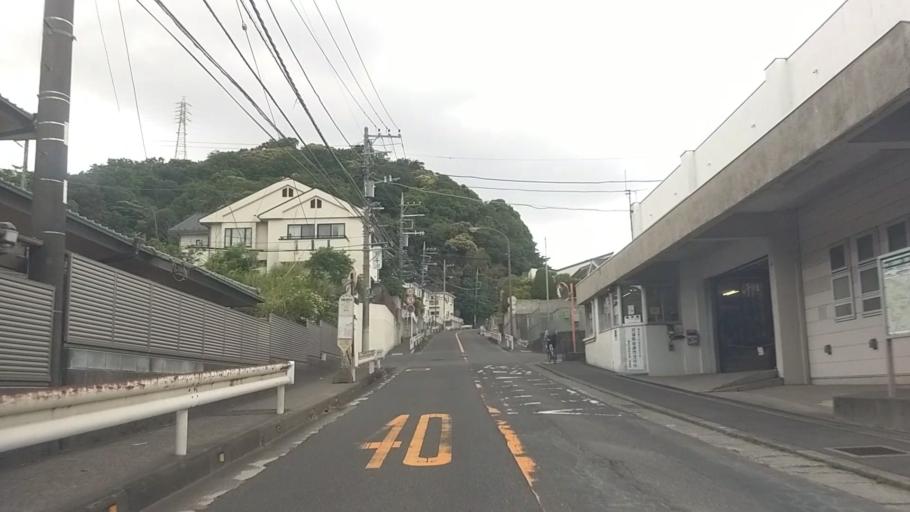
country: JP
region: Kanagawa
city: Kamakura
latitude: 35.3544
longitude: 139.5243
